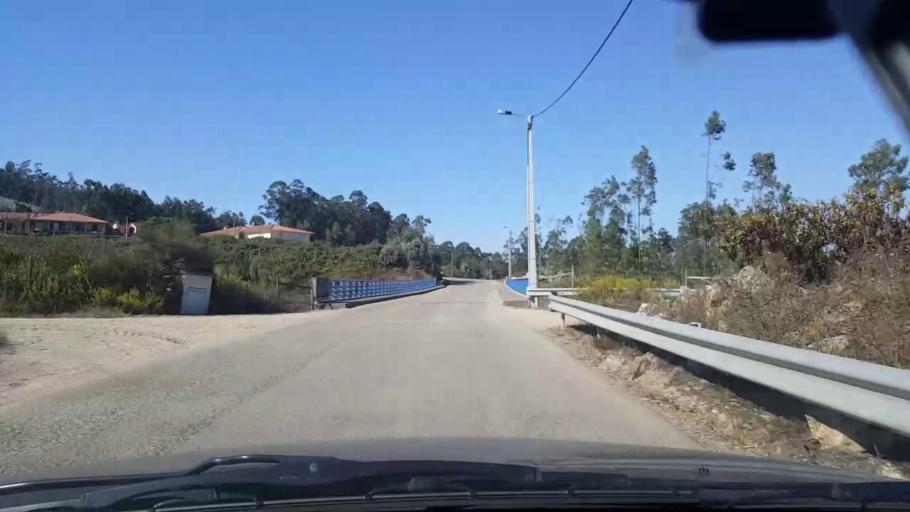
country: PT
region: Braga
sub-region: Vila Nova de Famalicao
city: Ribeirao
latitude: 41.3812
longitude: -8.6399
